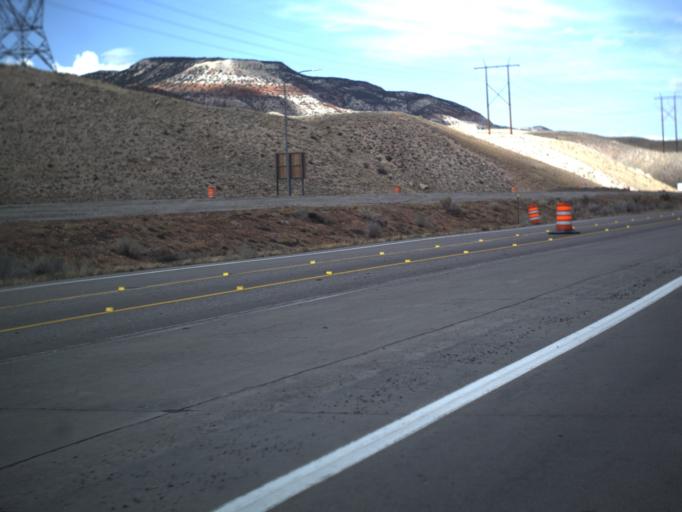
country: US
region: Utah
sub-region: Sevier County
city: Richfield
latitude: 38.7922
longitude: -112.0779
